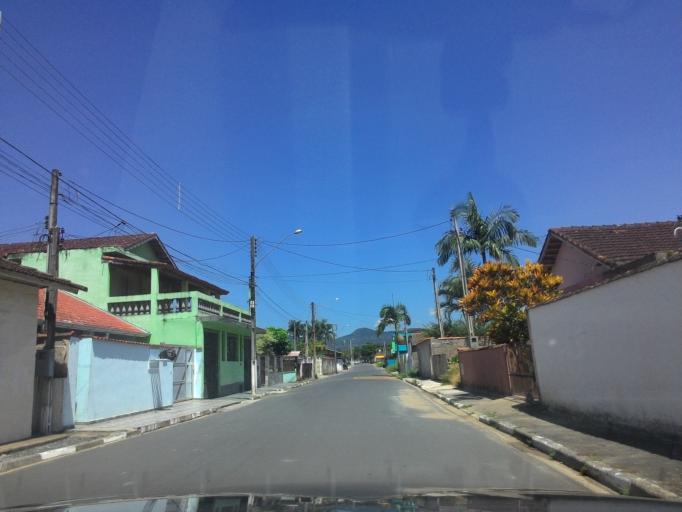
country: BR
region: Sao Paulo
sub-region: Pariquera-Acu
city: Pariquera Acu
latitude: -24.7124
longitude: -47.8853
